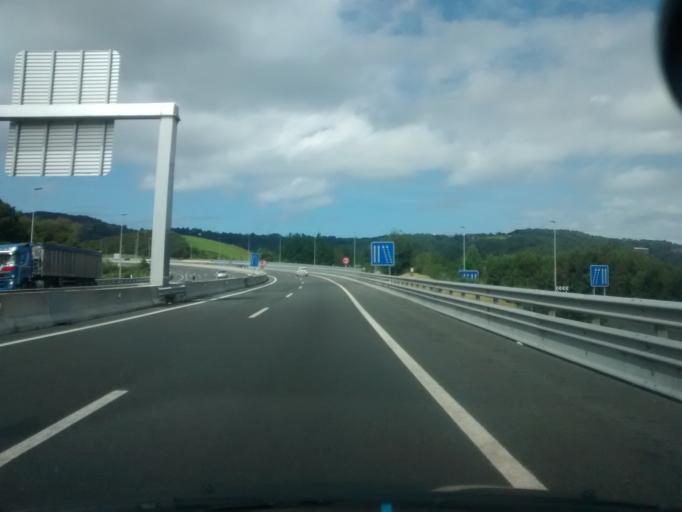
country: ES
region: Basque Country
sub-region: Provincia de Guipuzcoa
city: Usurbil
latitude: 43.2900
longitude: -2.0370
